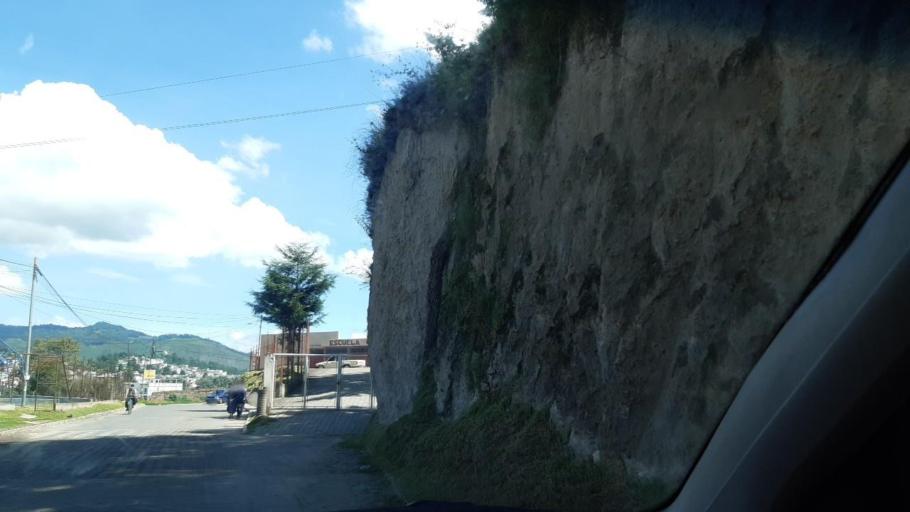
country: GT
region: Quetzaltenango
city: Salcaja
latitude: 14.8725
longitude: -91.4580
